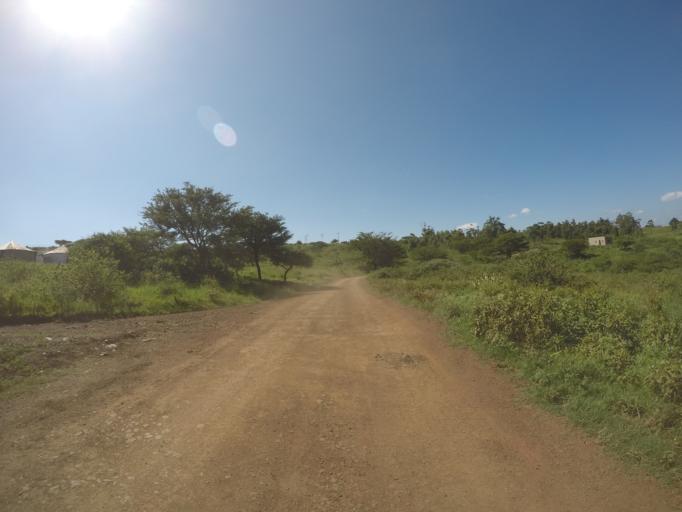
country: ZA
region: KwaZulu-Natal
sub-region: uThungulu District Municipality
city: Empangeni
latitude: -28.5658
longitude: 31.6989
